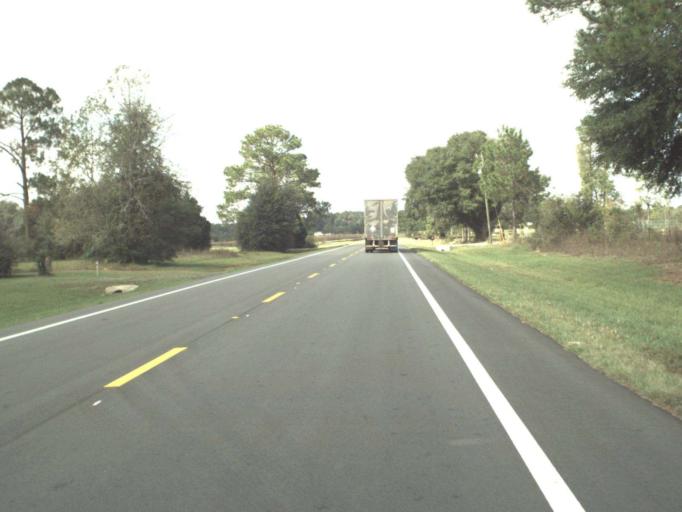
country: US
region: Florida
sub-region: Jackson County
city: Malone
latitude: 30.9773
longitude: -85.1725
